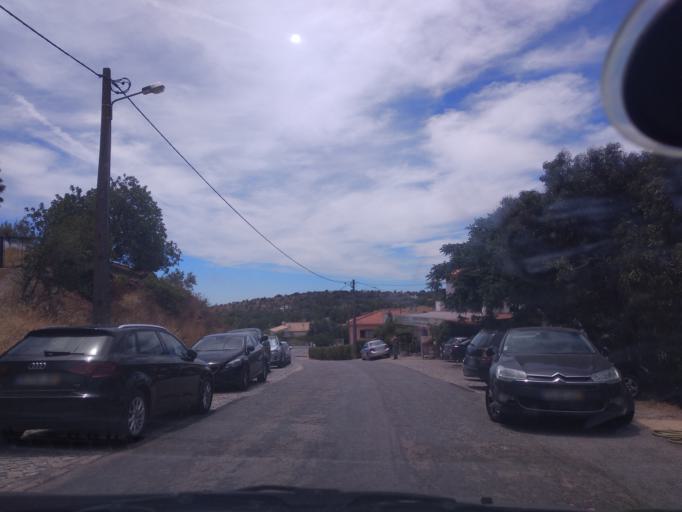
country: PT
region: Faro
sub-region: Olhao
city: Moncarapacho
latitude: 37.1543
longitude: -7.7959
